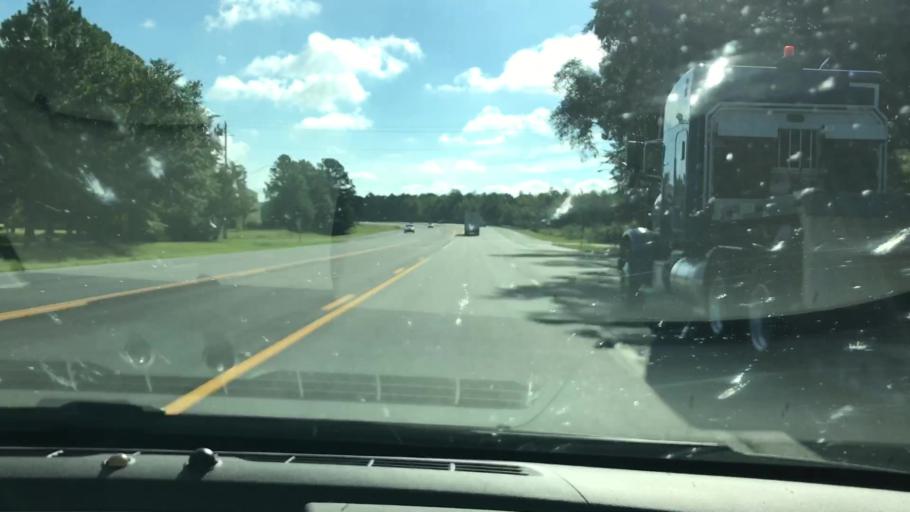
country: US
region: Georgia
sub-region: Dougherty County
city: Albany
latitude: 31.5801
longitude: -84.0741
